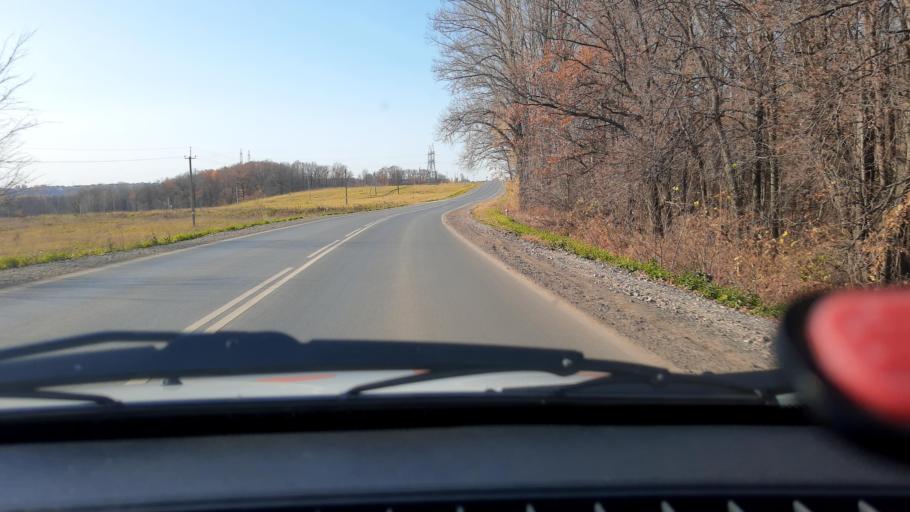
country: RU
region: Bashkortostan
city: Mikhaylovka
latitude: 54.8331
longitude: 55.9322
